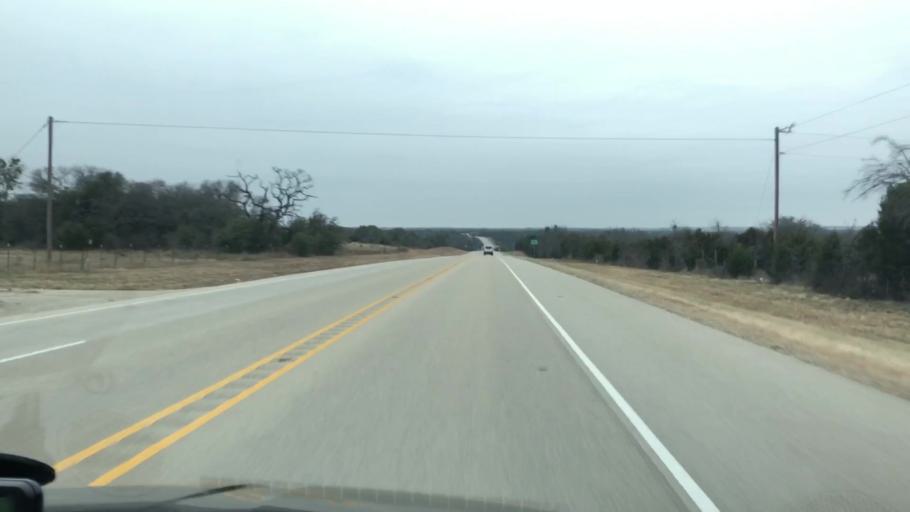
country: US
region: Texas
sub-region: Hamilton County
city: Hamilton
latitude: 31.5740
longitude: -98.1579
